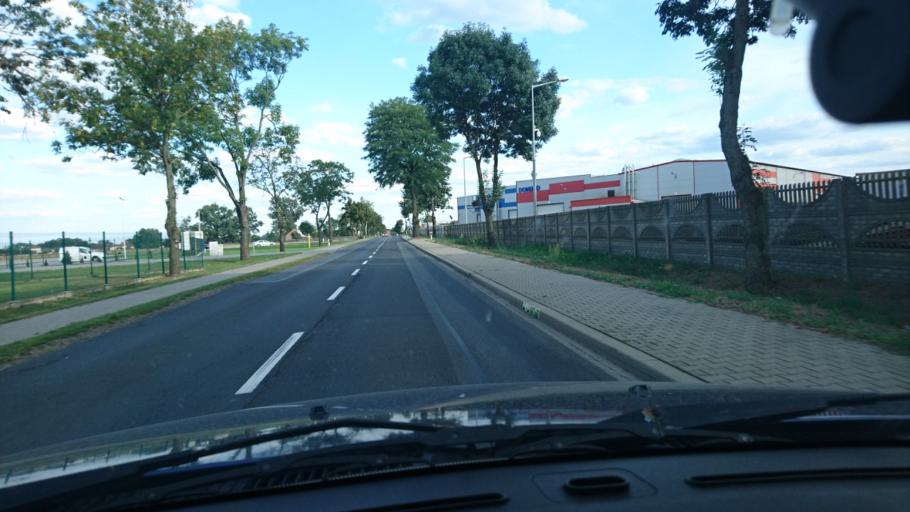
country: PL
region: Greater Poland Voivodeship
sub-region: Powiat ostrowski
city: Odolanow
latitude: 51.5860
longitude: 17.6506
